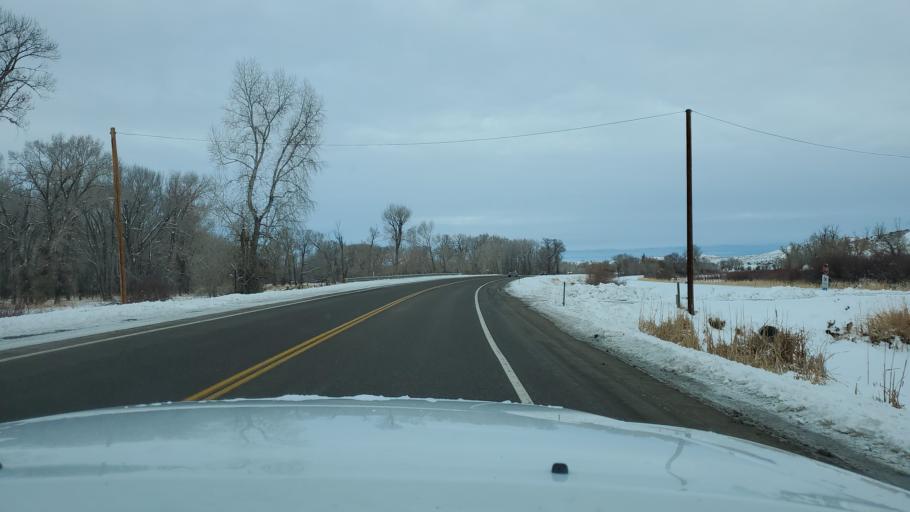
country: US
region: Colorado
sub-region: Routt County
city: Hayden
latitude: 40.4945
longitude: -107.3690
